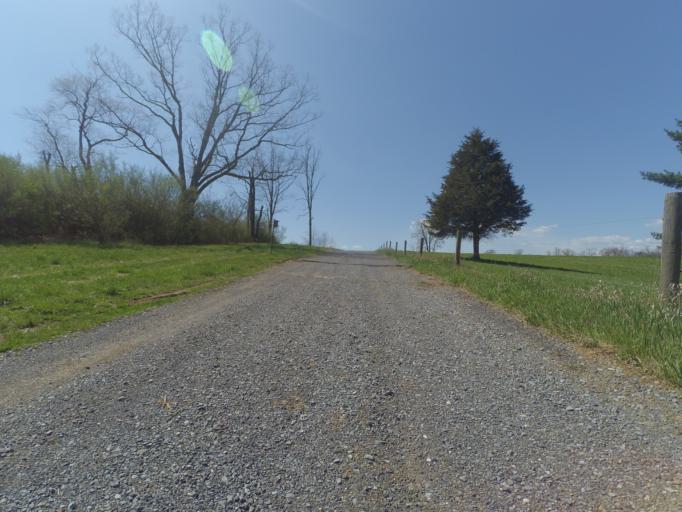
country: US
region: Pennsylvania
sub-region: Centre County
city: Houserville
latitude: 40.8313
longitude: -77.8489
